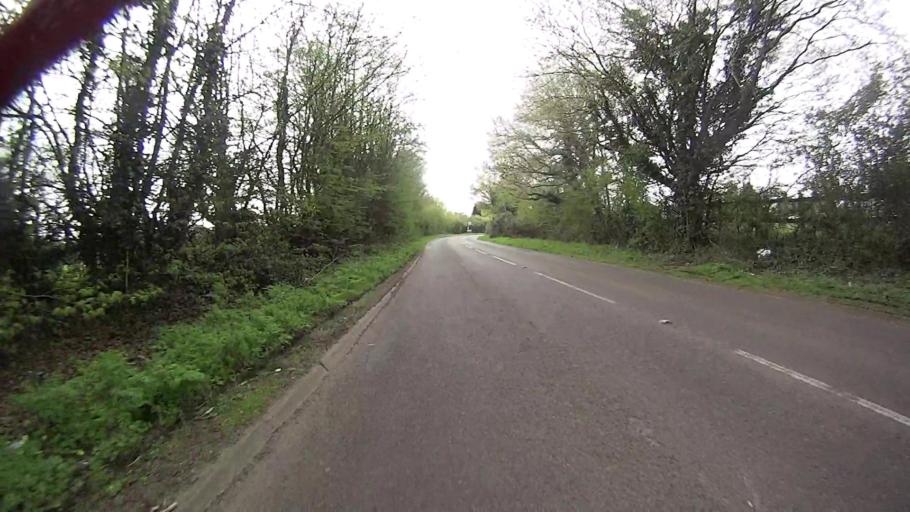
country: GB
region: England
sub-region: Surrey
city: Newdigate
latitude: 51.1264
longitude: -0.2794
